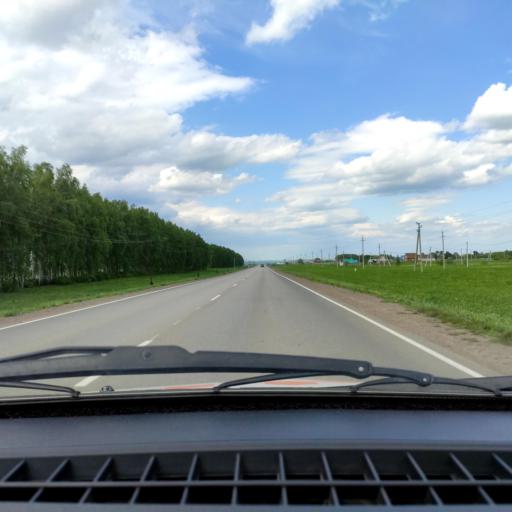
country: RU
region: Bashkortostan
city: Iglino
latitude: 54.9989
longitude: 56.4998
